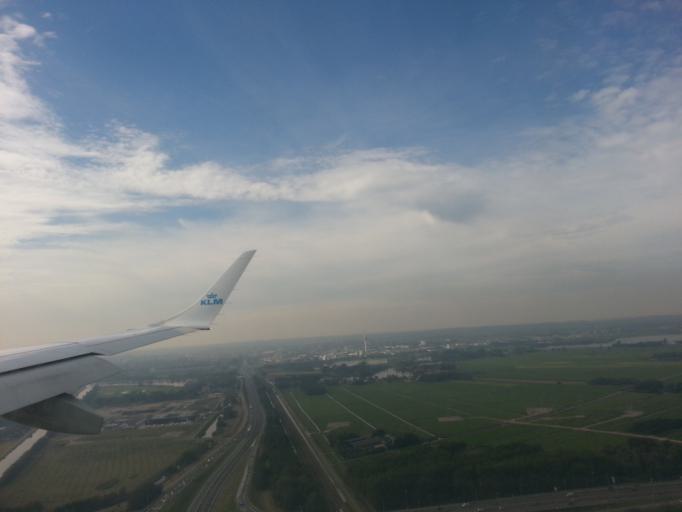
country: NL
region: North Holland
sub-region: Gemeente Haarlem
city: Haarlem
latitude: 52.3854
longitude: 4.7141
